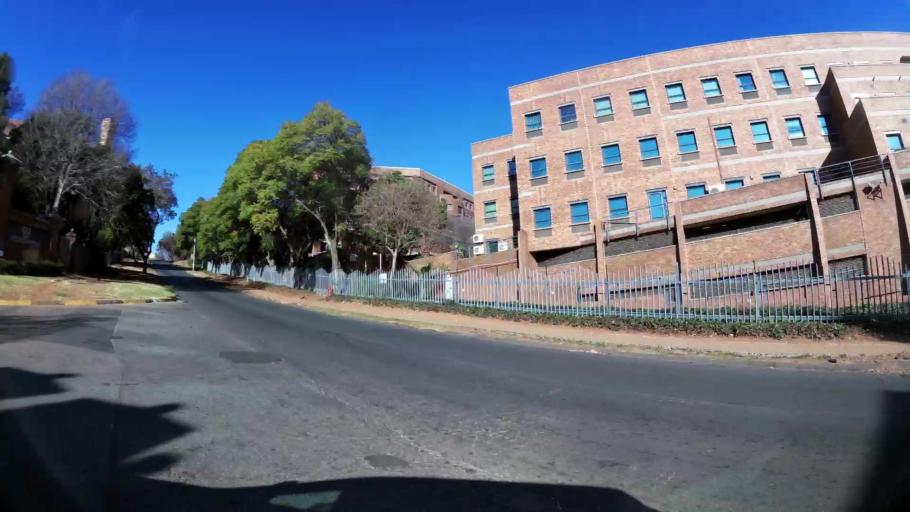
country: ZA
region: Gauteng
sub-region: City of Johannesburg Metropolitan Municipality
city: Johannesburg
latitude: -26.1788
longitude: 28.0494
